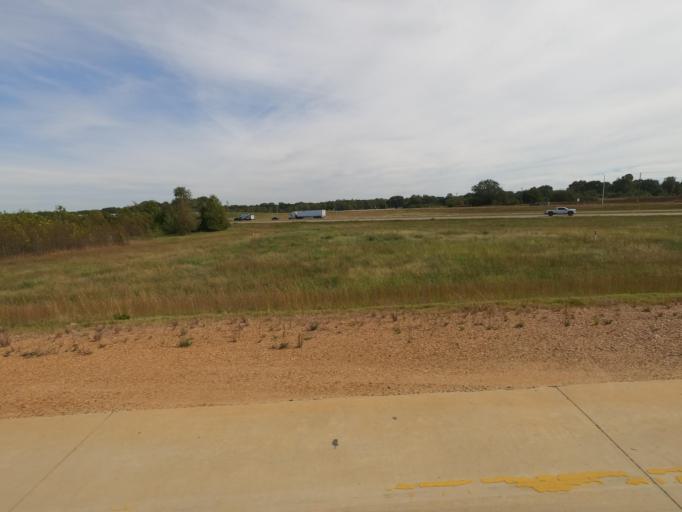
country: US
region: Tennessee
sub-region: Shelby County
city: Arlington
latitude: 35.2908
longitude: -89.6134
